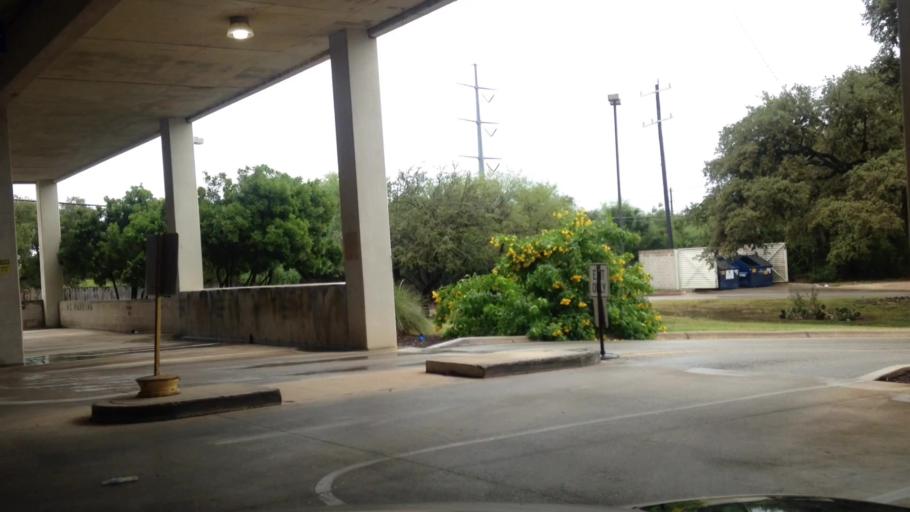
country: US
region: Texas
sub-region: Bexar County
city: Hollywood Park
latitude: 29.6190
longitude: -98.4905
